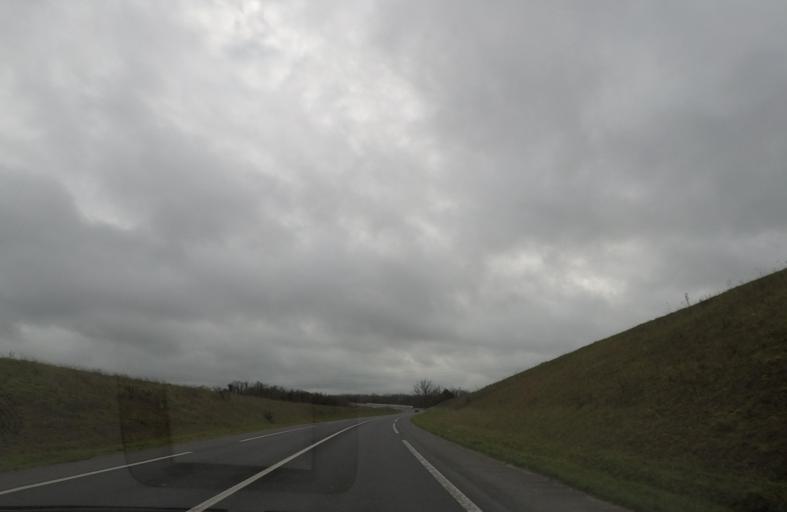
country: FR
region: Centre
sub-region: Departement du Loir-et-Cher
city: Naveil
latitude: 47.7773
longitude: 1.0289
